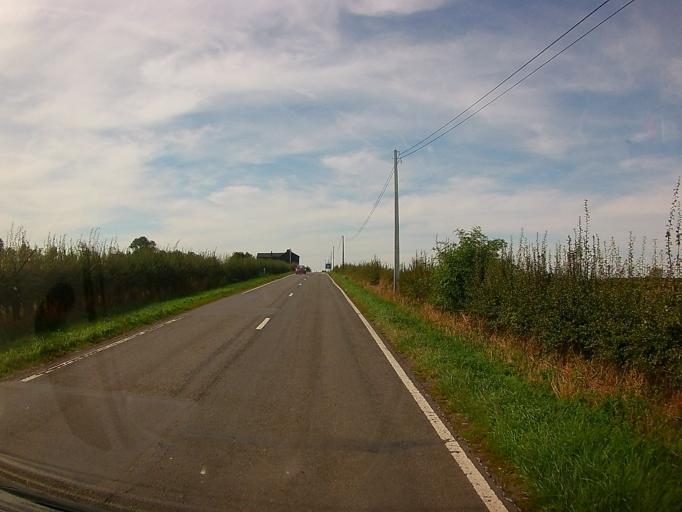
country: BE
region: Wallonia
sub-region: Province de Liege
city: Aubel
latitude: 50.7101
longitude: 5.8919
